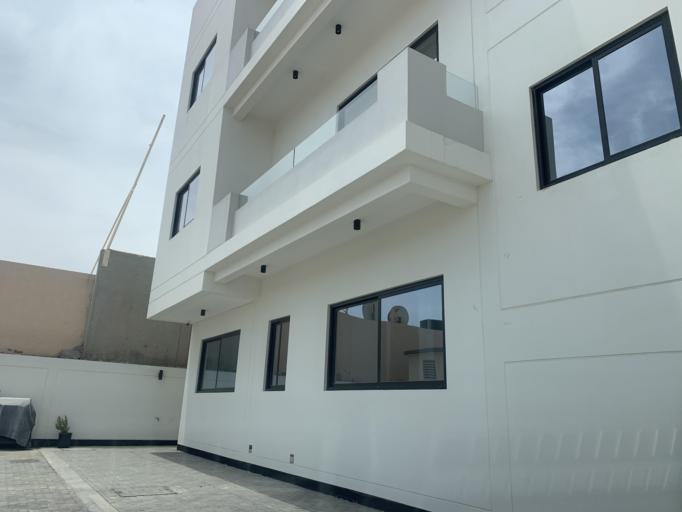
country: BH
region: Central Governorate
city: Madinat Hamad
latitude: 26.1801
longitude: 50.4757
